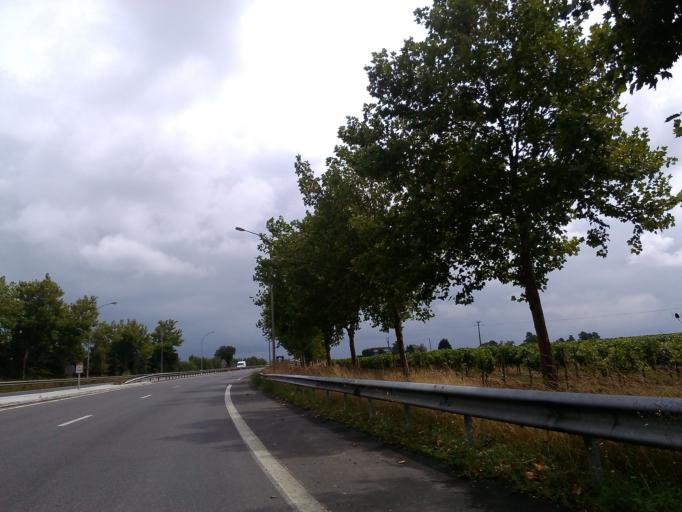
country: FR
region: Poitou-Charentes
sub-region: Departement de la Charente
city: Saint-Brice
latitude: 45.6813
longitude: -0.2917
